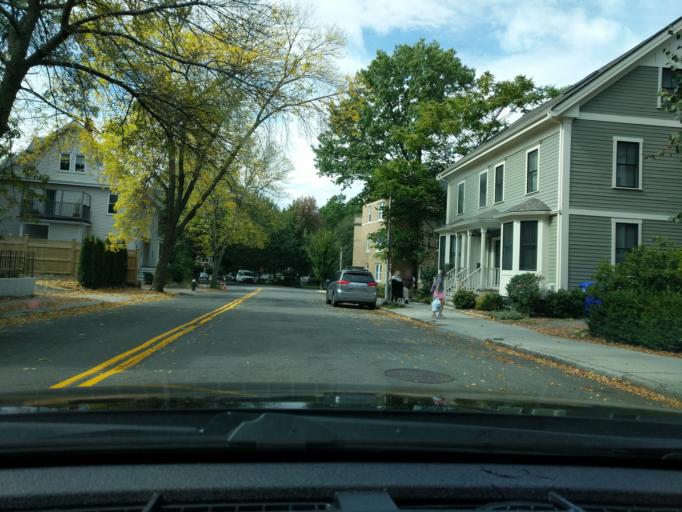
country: US
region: Massachusetts
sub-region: Norfolk County
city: Brookline
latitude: 42.3475
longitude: -71.1194
